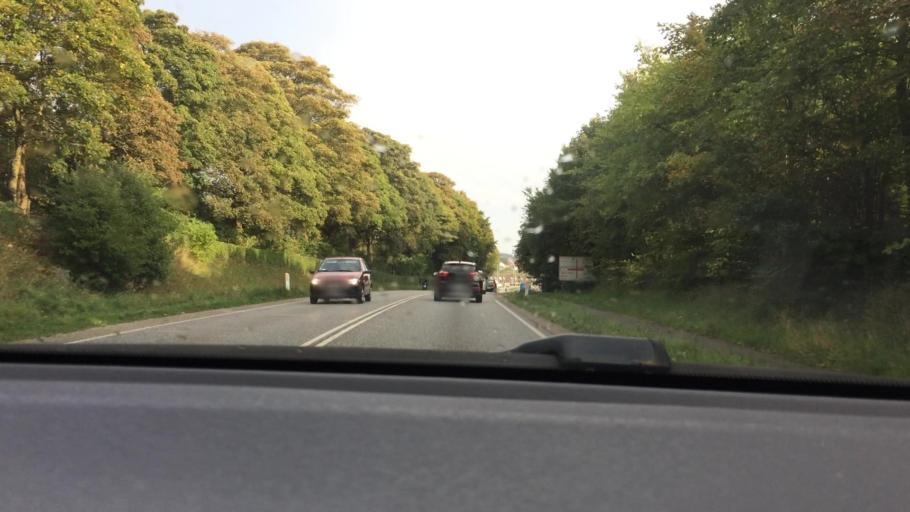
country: DK
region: Central Jutland
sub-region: Horsens Kommune
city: Horsens
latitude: 55.8765
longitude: 9.8176
